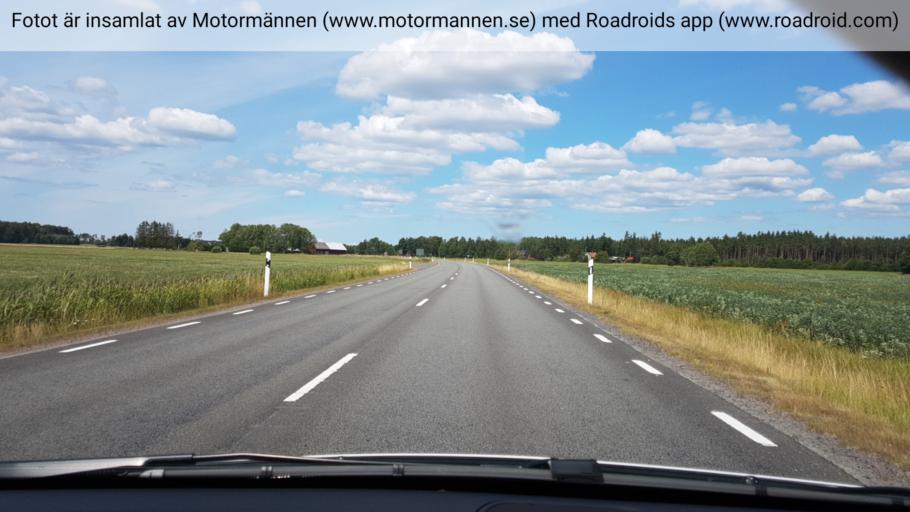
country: SE
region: Vaestra Goetaland
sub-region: Mariestads Kommun
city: Mariestad
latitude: 58.6388
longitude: 13.9152
